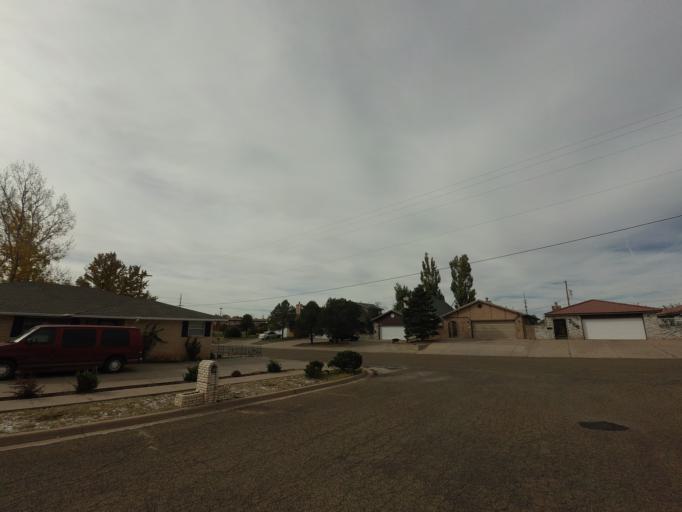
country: US
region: New Mexico
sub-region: Curry County
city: Clovis
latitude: 34.4204
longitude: -103.2114
